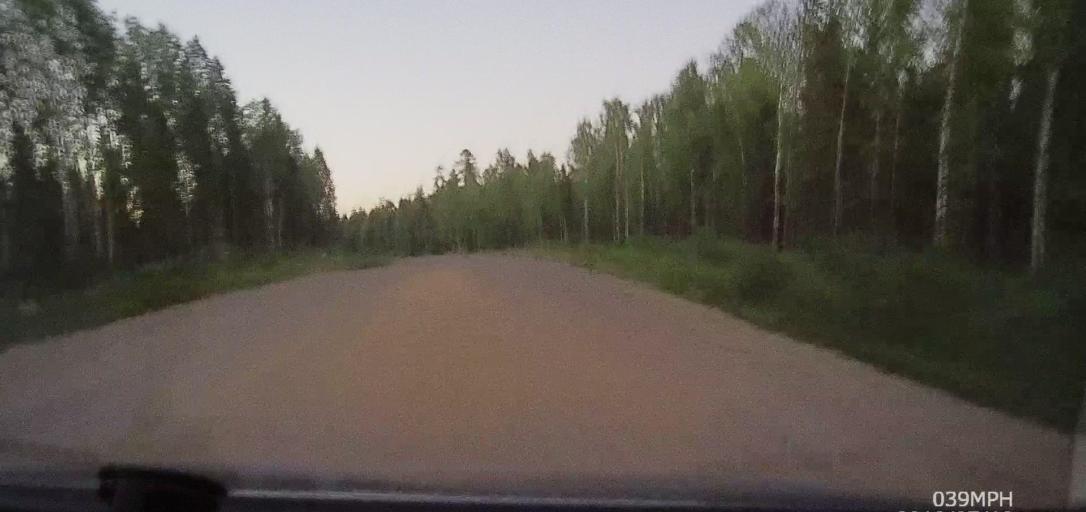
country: RU
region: Arkhangelskaya
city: Pinega
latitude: 64.4343
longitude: 43.1376
